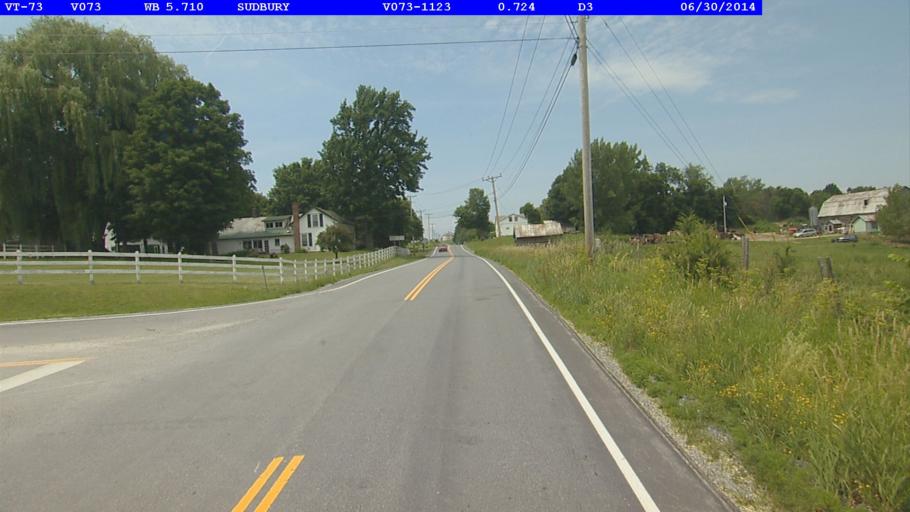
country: US
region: Vermont
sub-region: Rutland County
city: Brandon
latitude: 43.8236
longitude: -73.1861
